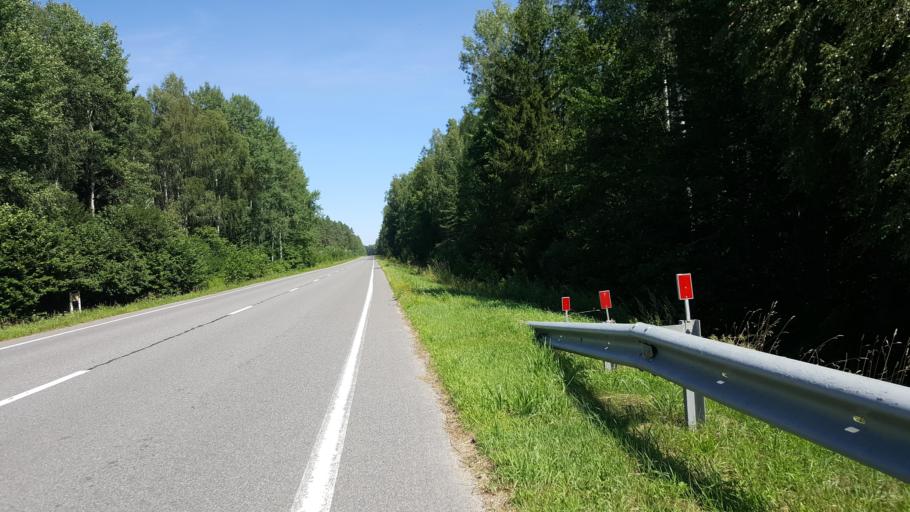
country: BY
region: Brest
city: Pruzhany
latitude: 52.5022
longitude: 24.1755
